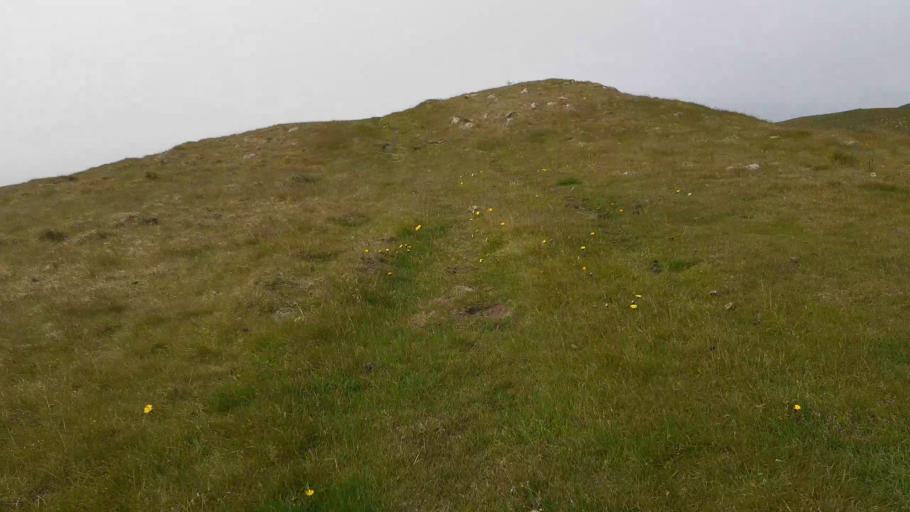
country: IS
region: Northeast
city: Dalvik
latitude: 66.5431
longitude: -17.9922
